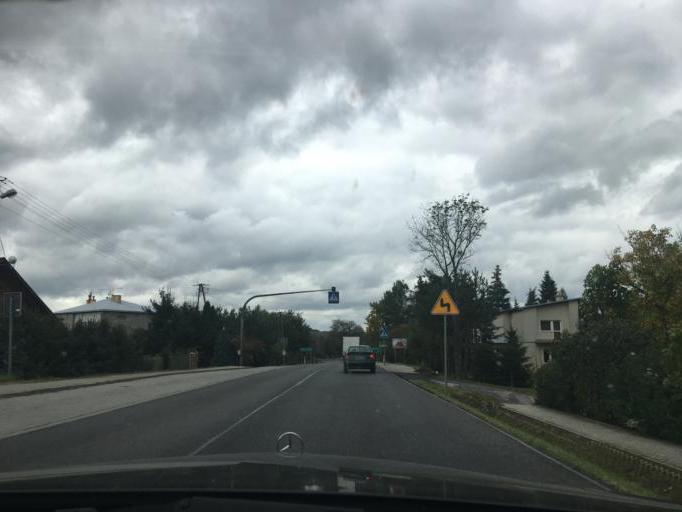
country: PL
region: Subcarpathian Voivodeship
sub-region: Powiat krosnienski
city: Kroscienko Wyzne
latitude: 49.6746
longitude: 21.8498
